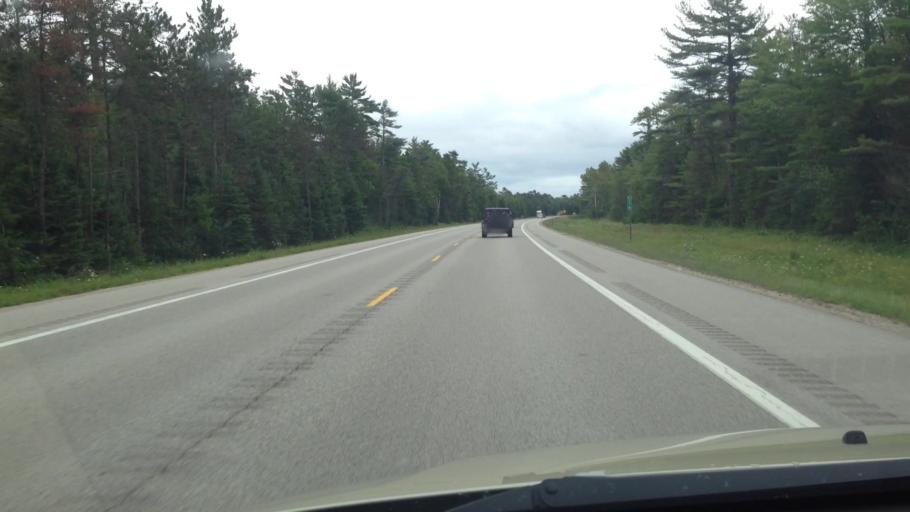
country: US
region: Michigan
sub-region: Luce County
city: Newberry
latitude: 46.0998
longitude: -85.4891
